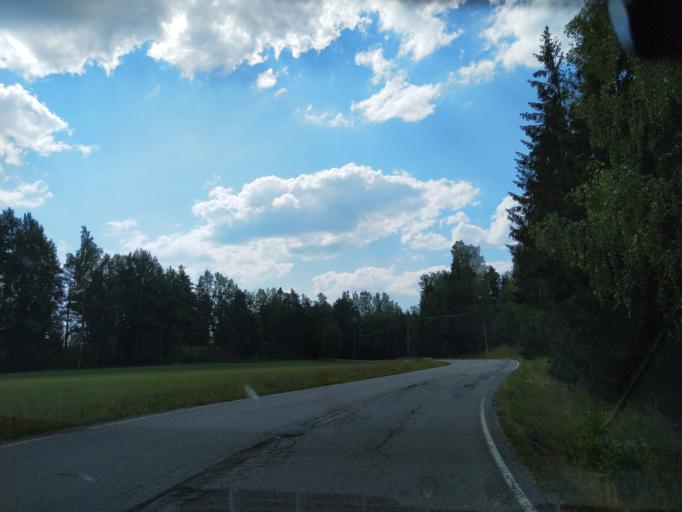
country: FI
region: Uusimaa
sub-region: Helsinki
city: Kirkkonummi
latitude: 60.0580
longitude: 24.4960
